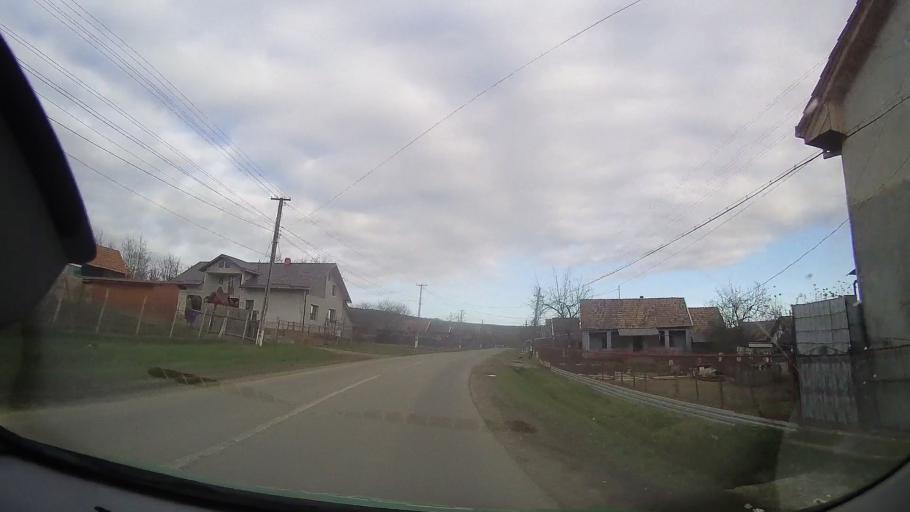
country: RO
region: Mures
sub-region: Comuna Iernut
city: Iernut
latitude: 46.4776
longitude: 24.2279
